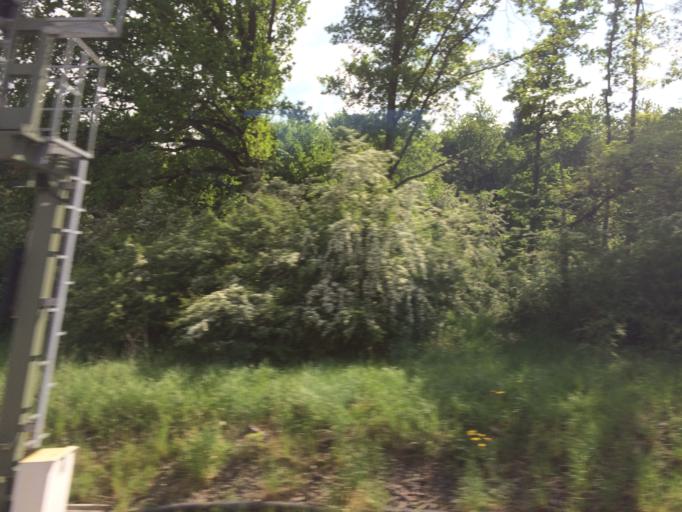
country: DE
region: Bavaria
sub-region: Regierungsbezirk Mittelfranken
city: Wilhelmsdorf
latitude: 49.5513
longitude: 10.7336
